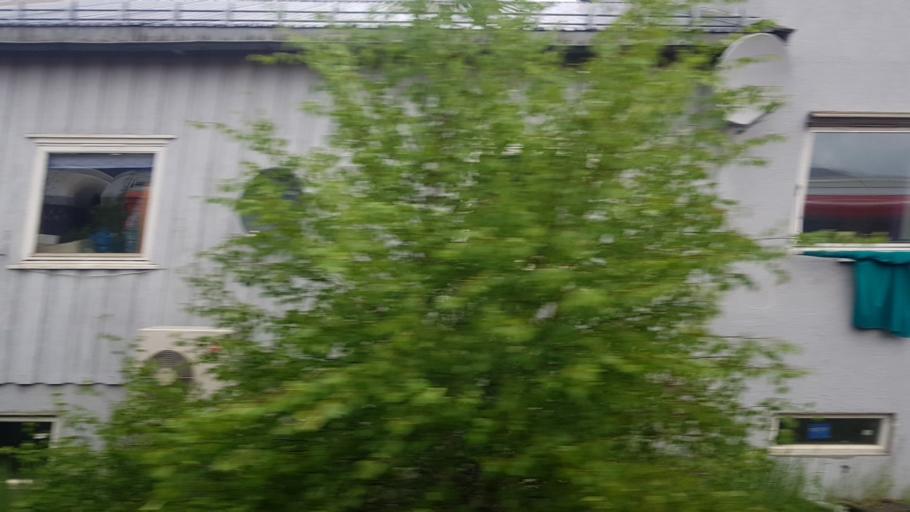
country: NO
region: Oppland
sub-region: Sor-Fron
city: Hundorp
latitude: 61.5632
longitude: 9.9199
